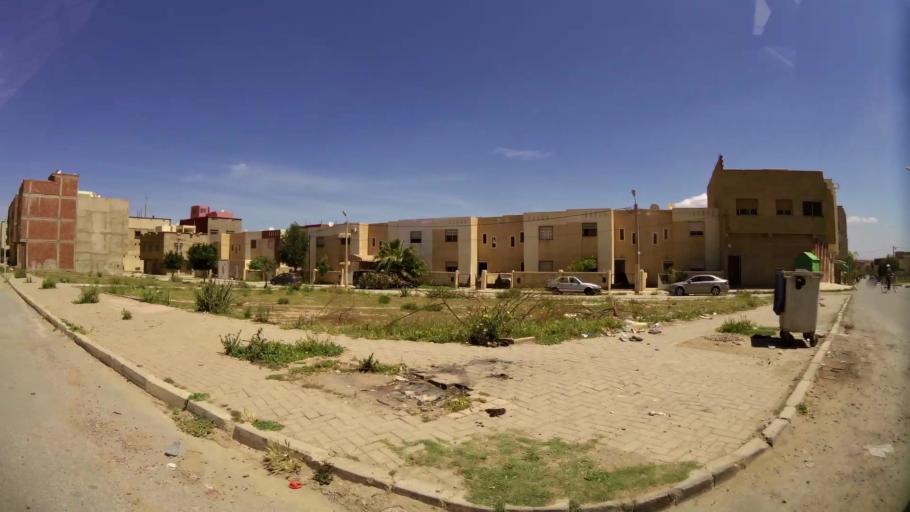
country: MA
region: Oriental
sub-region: Oujda-Angad
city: Oujda
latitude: 34.6596
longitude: -1.9465
